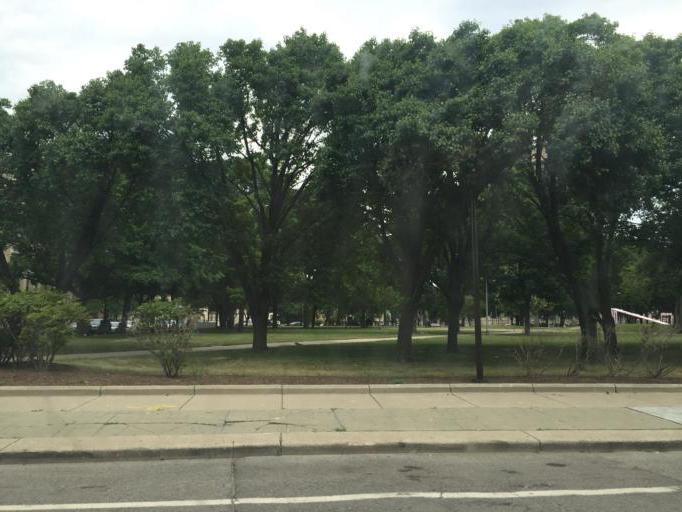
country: US
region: Michigan
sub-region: Wayne County
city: Detroit
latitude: 42.3396
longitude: -83.0606
